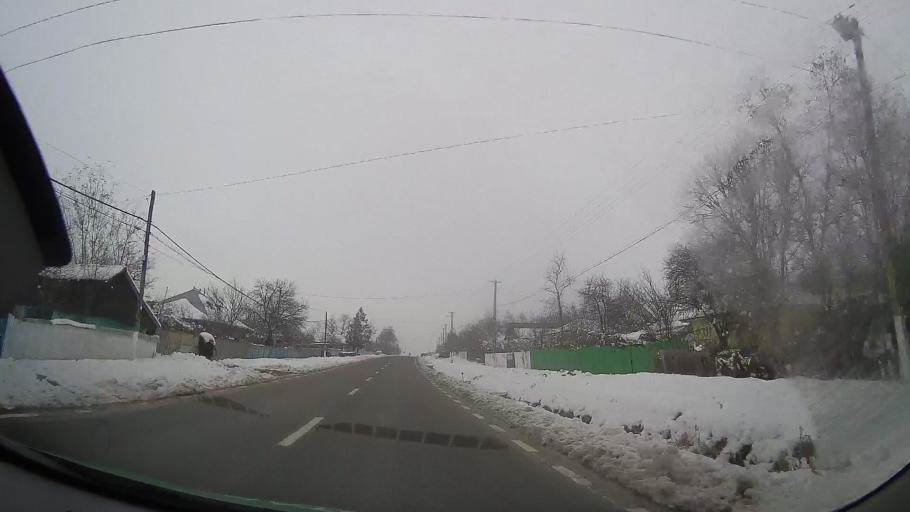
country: RO
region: Vaslui
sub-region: Comuna Stefan cel Mare
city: Stefan cel Mare
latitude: 46.7240
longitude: 27.6217
